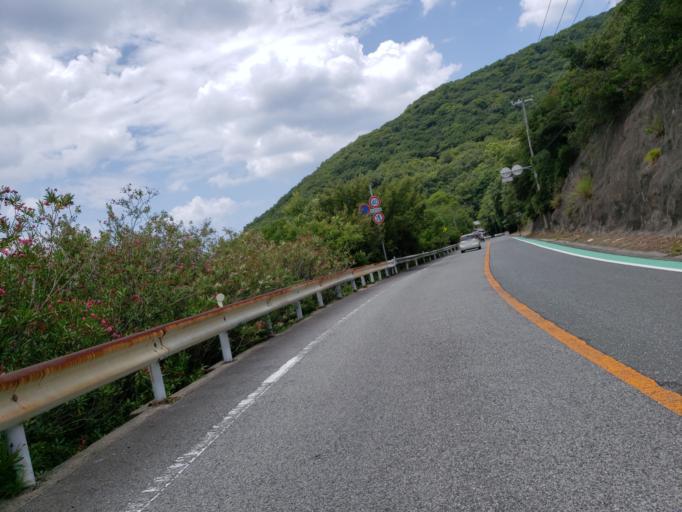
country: JP
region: Hyogo
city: Aioi
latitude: 34.7721
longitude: 134.5174
